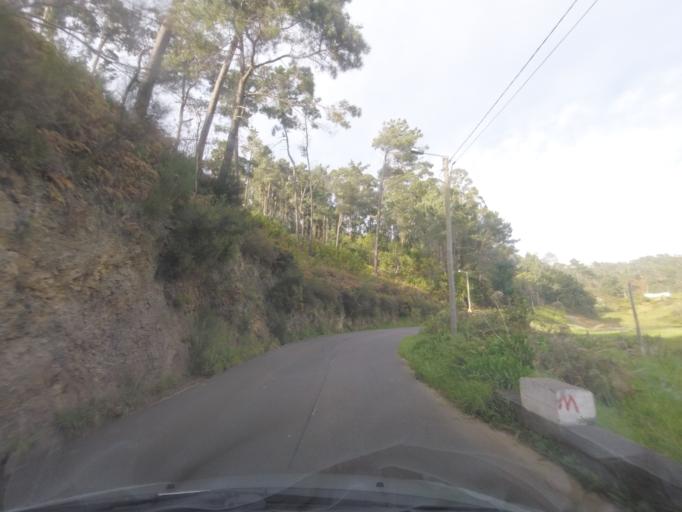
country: PT
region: Madeira
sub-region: Calheta
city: Faja da Ovelha
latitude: 32.7753
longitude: -17.2214
